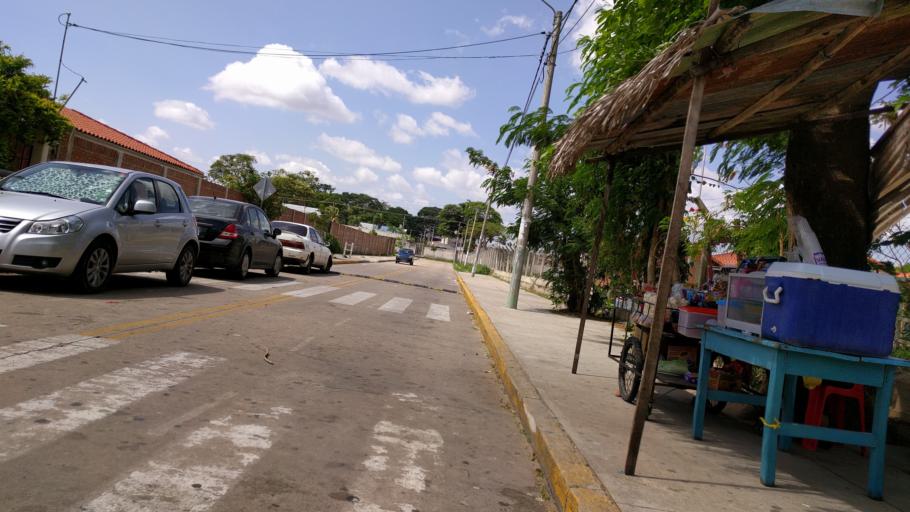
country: BO
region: Santa Cruz
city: Santa Cruz de la Sierra
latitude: -17.7814
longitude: -63.2097
